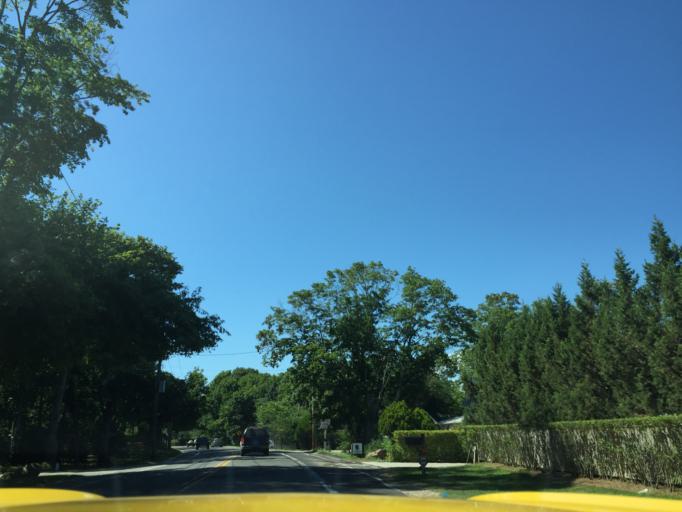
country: US
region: New York
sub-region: Suffolk County
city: Sag Harbor
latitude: 41.0101
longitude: -72.3057
